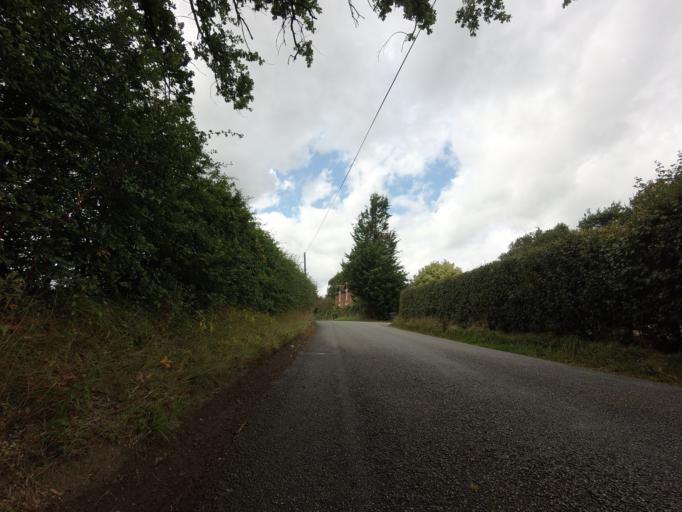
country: GB
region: England
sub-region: Kent
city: Hadlow
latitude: 51.2459
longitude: 0.3122
